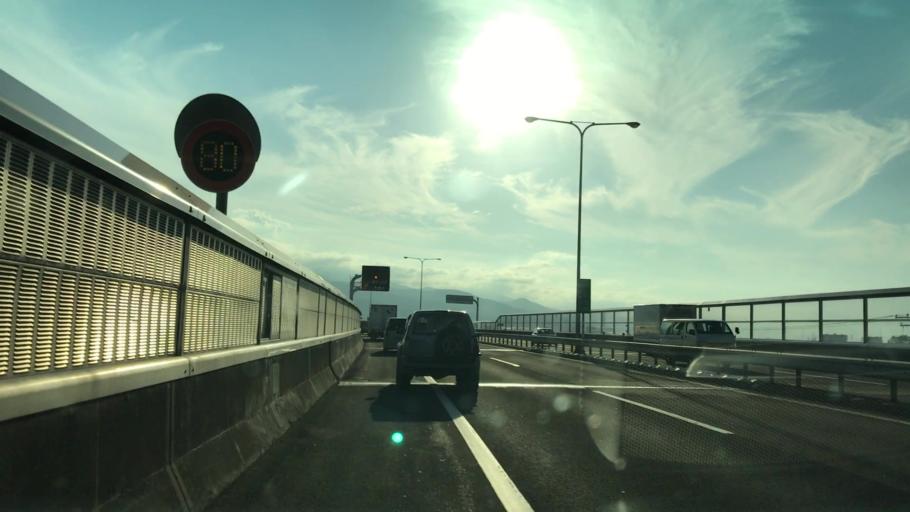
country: JP
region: Hokkaido
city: Sapporo
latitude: 43.1030
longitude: 141.3194
